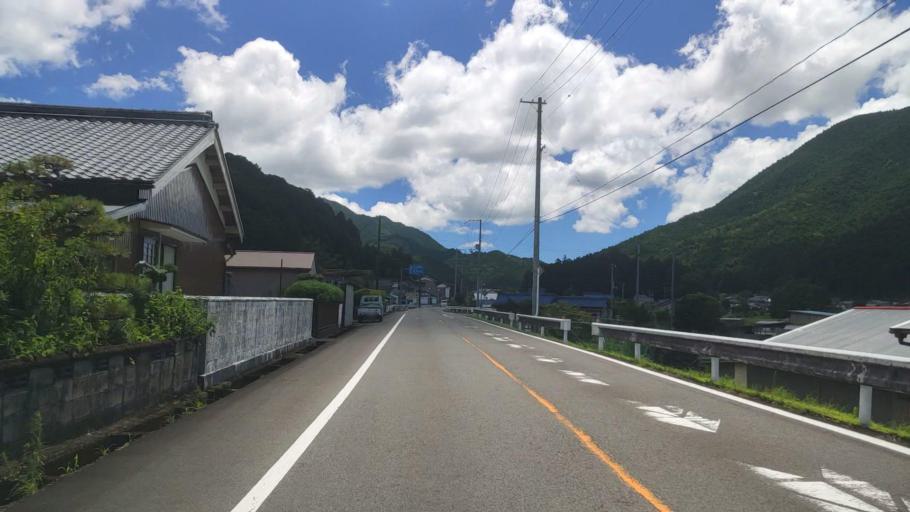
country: JP
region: Mie
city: Owase
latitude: 33.9804
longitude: 136.0498
